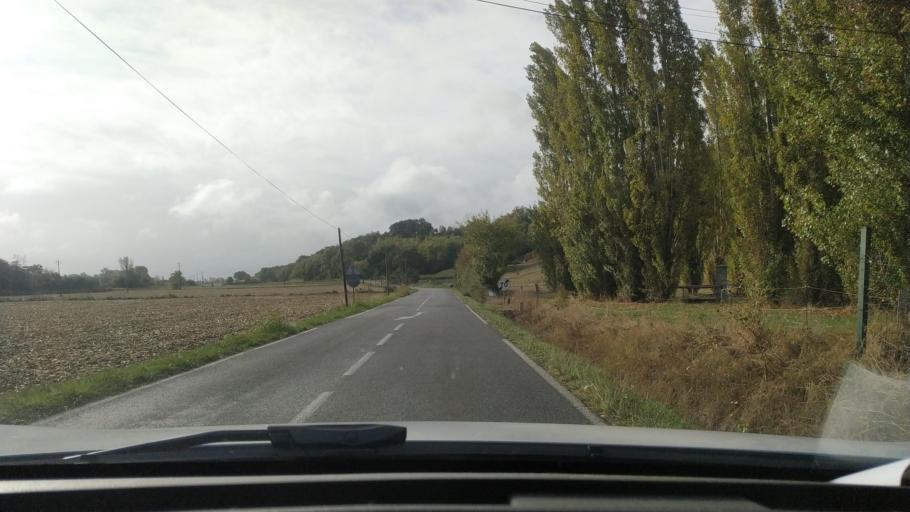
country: FR
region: Midi-Pyrenees
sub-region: Departement de la Haute-Garonne
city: Auterive
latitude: 43.3152
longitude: 1.4563
